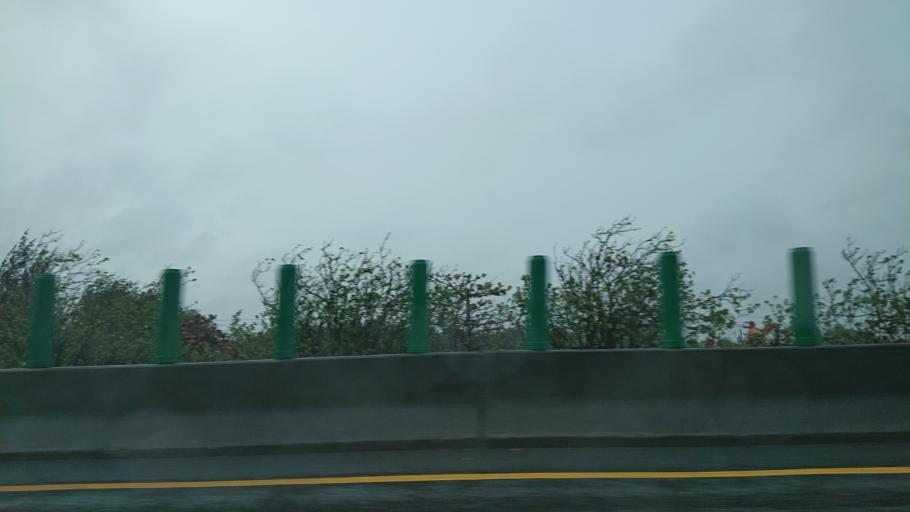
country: TW
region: Taiwan
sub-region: Chiayi
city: Taibao
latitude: 23.7249
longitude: 120.2181
